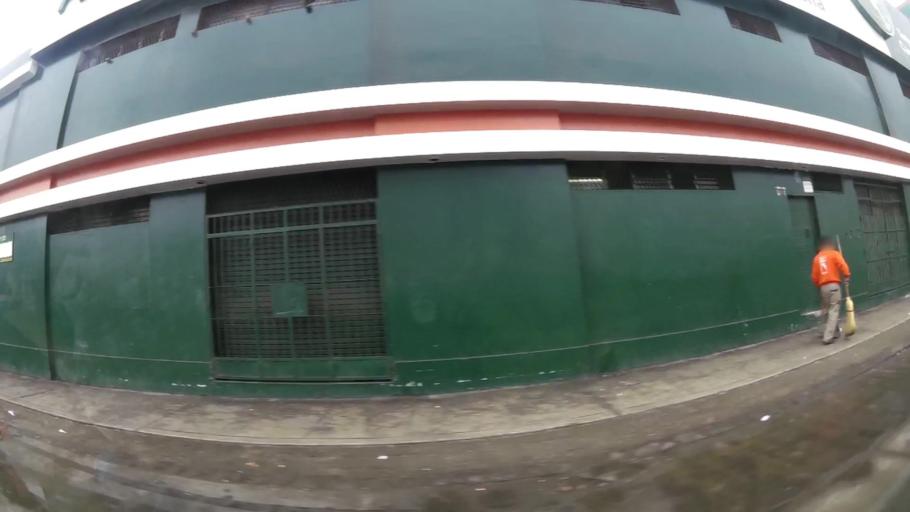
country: PE
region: Lima
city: Lima
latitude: -12.0638
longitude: -77.0532
